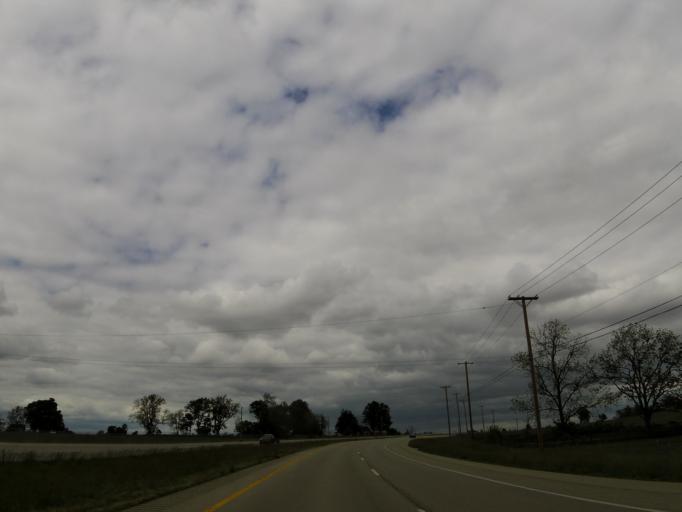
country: US
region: Kentucky
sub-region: Scott County
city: Georgetown
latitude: 38.1627
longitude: -84.6094
